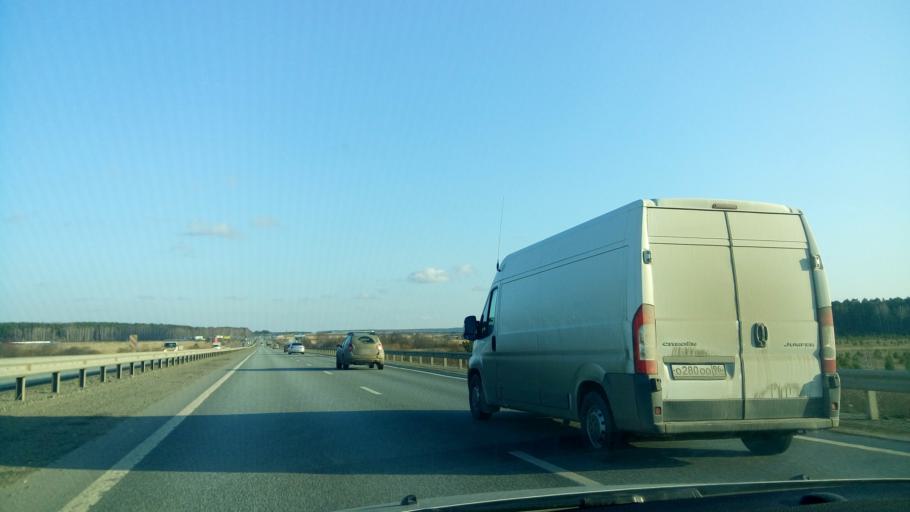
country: RU
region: Sverdlovsk
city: Bobrovskiy
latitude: 56.7540
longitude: 60.9525
